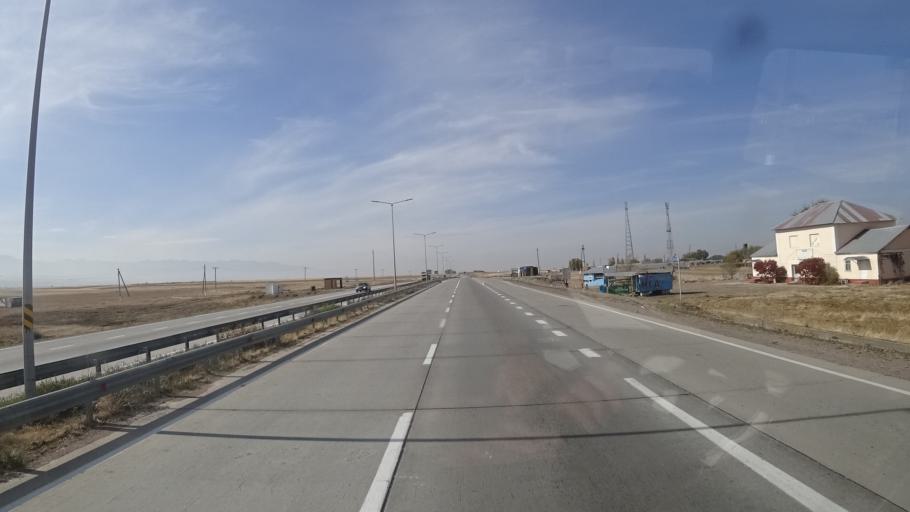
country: KZ
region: Zhambyl
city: Merke
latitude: 42.8892
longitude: 72.9869
